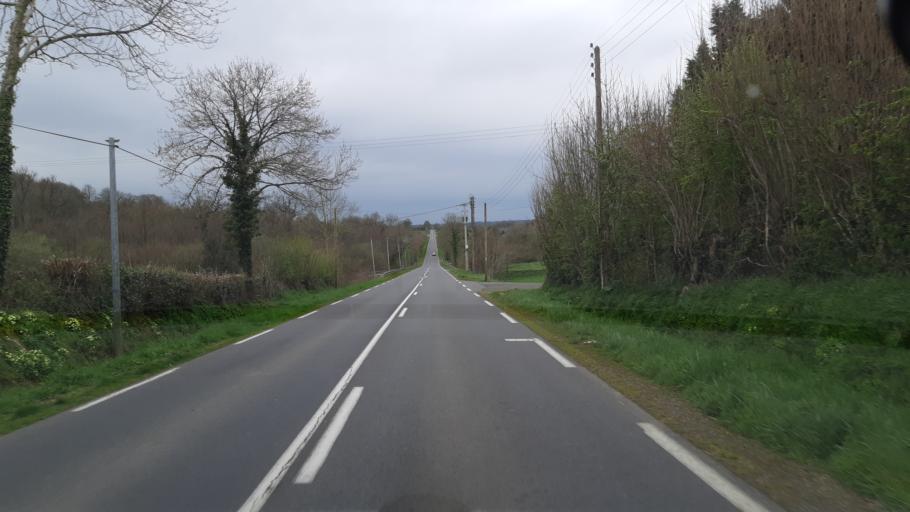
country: FR
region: Lower Normandy
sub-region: Departement de la Manche
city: Hambye
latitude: 48.9534
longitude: -1.2254
